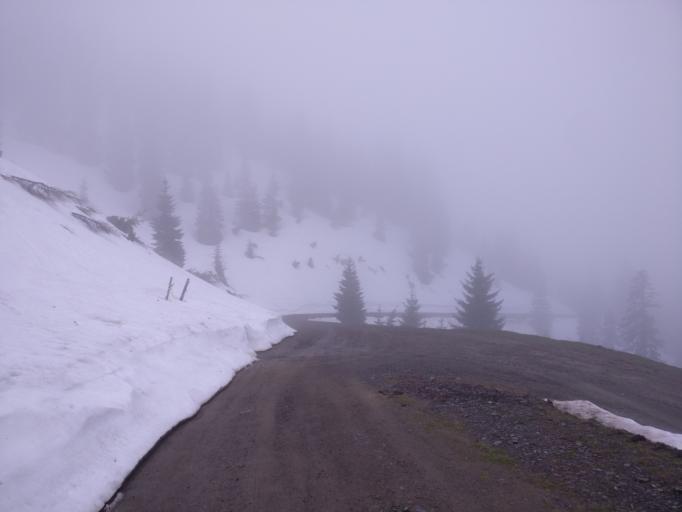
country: AT
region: Salzburg
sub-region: Politischer Bezirk Sankt Johann im Pongau
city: Werfenweng
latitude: 47.4736
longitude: 13.2999
